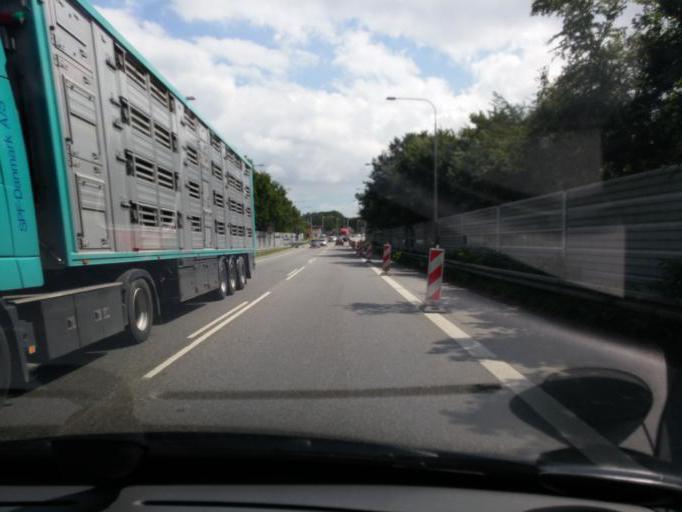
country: DK
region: South Denmark
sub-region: Svendborg Kommune
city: Vindeby
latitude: 55.0427
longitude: 10.6093
